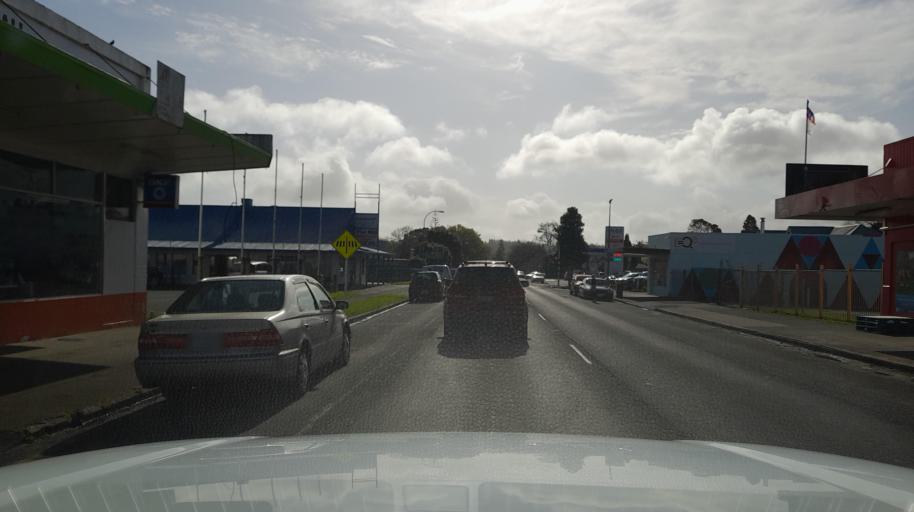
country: NZ
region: Northland
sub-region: Far North District
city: Waimate North
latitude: -35.4060
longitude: 173.8035
